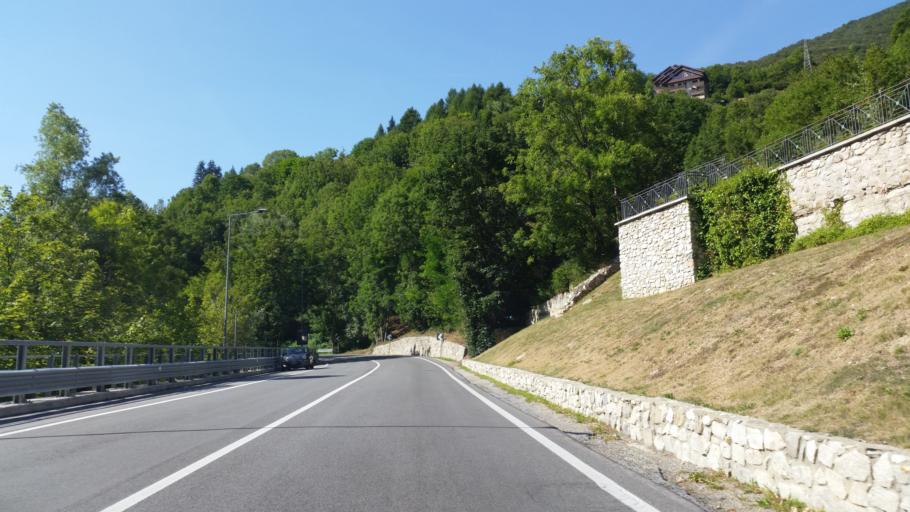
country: IT
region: Piedmont
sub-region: Provincia di Cuneo
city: Limone Piemonte
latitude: 44.2042
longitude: 7.5743
